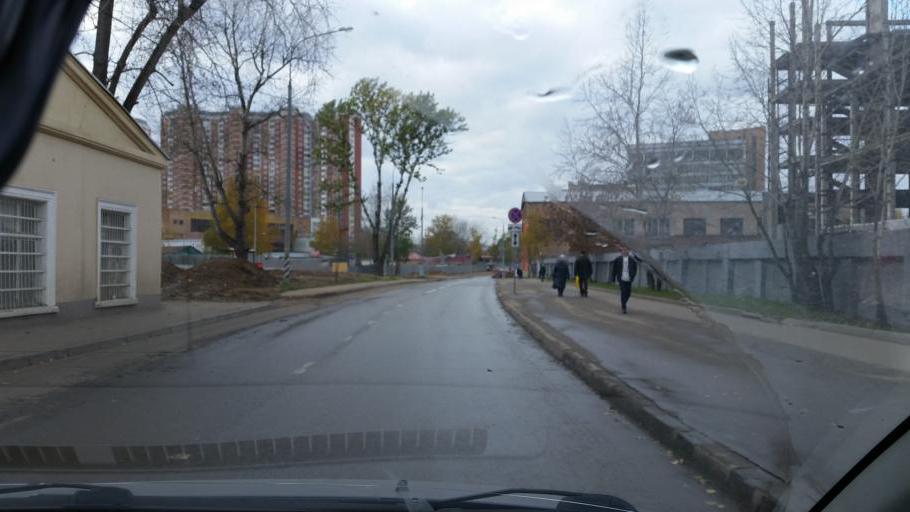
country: RU
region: Moscow
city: Kotlovka
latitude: 55.6730
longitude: 37.6177
